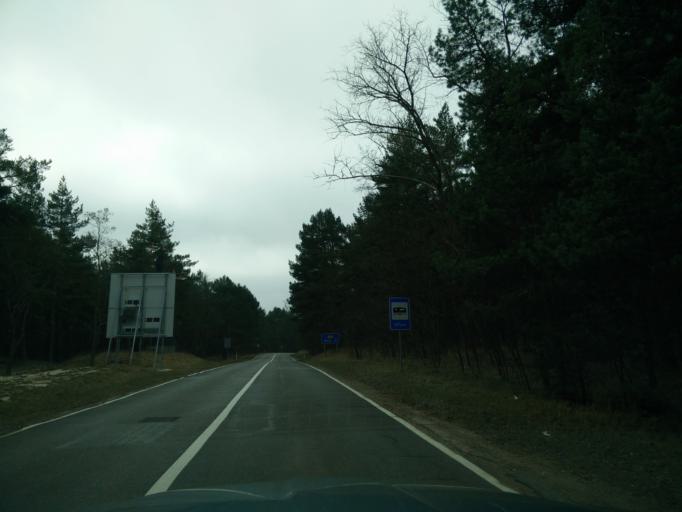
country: LT
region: Klaipedos apskritis
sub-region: Klaipeda
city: Klaipeda
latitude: 55.6778
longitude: 21.1132
